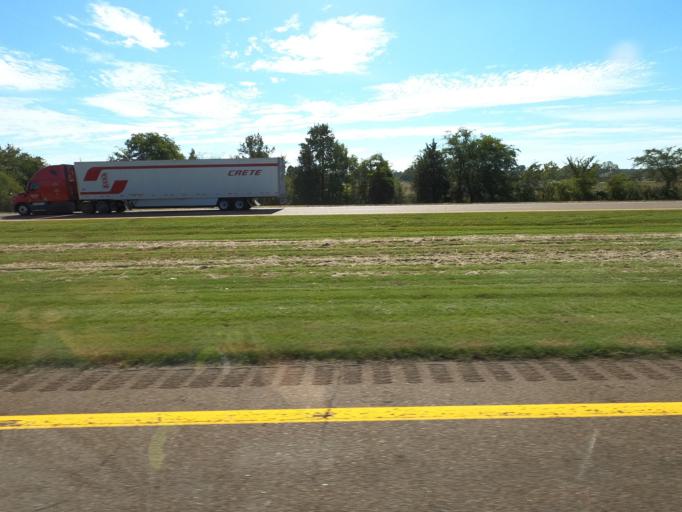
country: US
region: Tennessee
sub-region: Dyer County
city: Dyersburg
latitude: 36.0684
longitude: -89.3740
